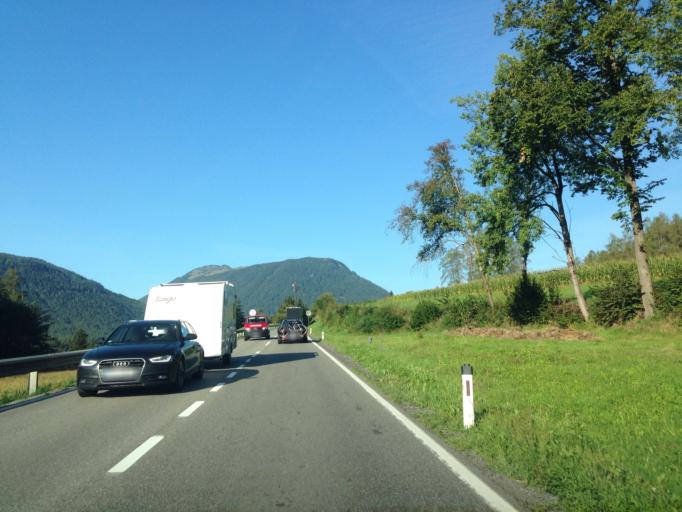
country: AT
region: Tyrol
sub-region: Politischer Bezirk Imst
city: Motz
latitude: 47.3007
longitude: 10.9531
